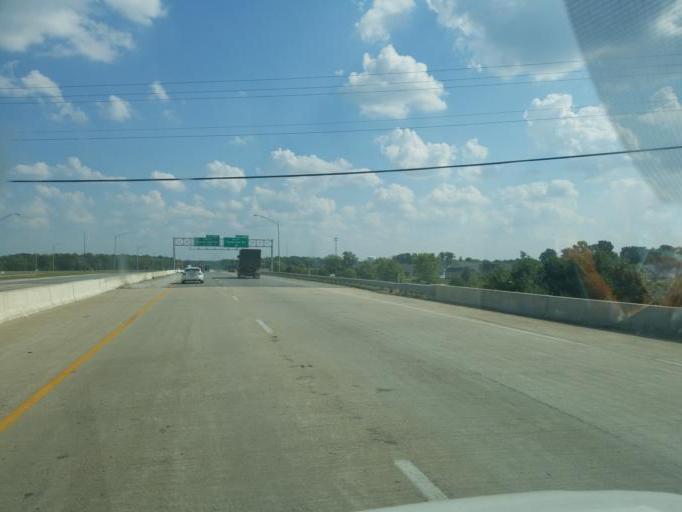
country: US
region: Indiana
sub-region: Allen County
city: Fort Wayne
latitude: 41.1618
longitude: -85.0700
